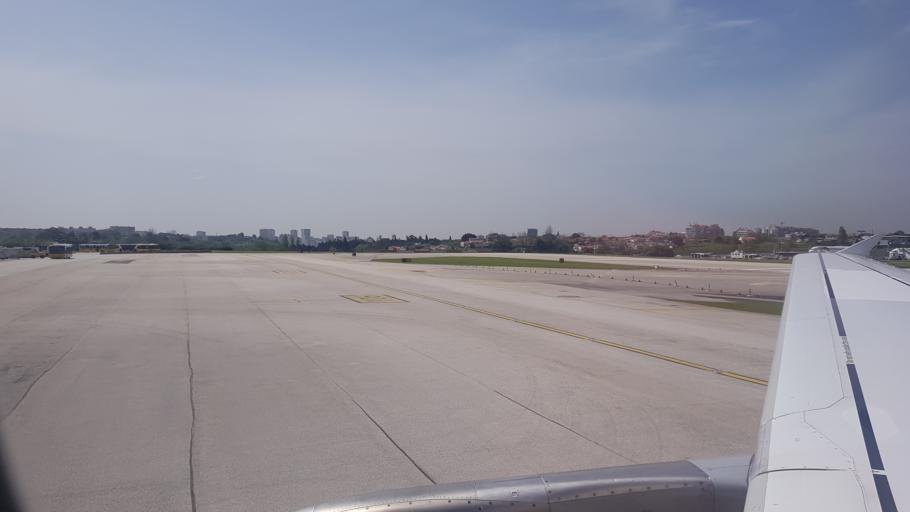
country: PT
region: Lisbon
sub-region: Loures
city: Moscavide
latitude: 38.7675
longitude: -9.1309
